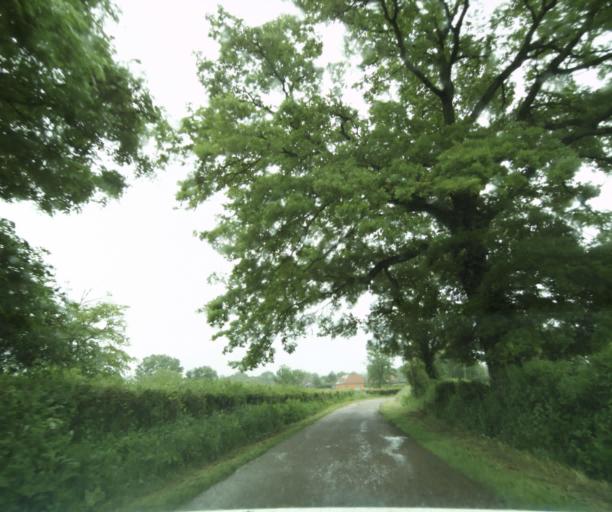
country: FR
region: Bourgogne
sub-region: Departement de Saone-et-Loire
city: Charolles
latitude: 46.4259
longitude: 4.3379
